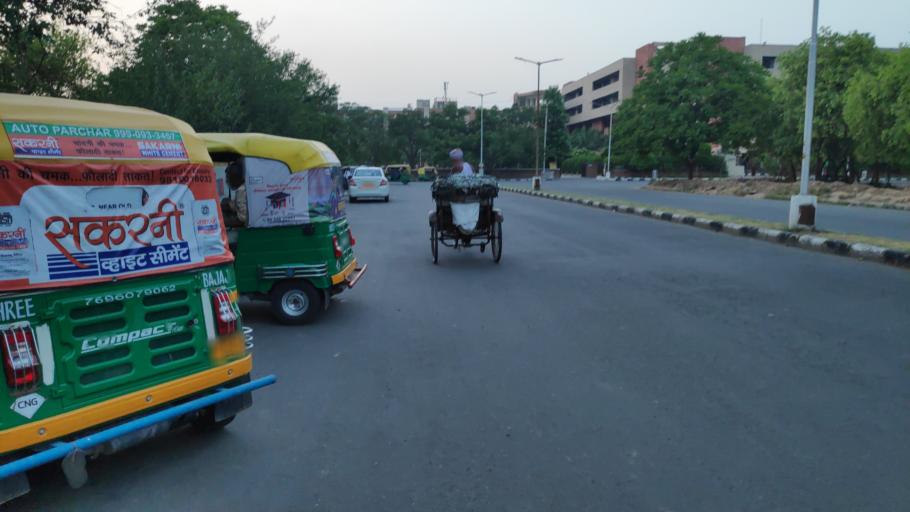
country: IN
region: Punjab
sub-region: Ajitgarh
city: Mohali
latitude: 30.7180
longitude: 76.7446
